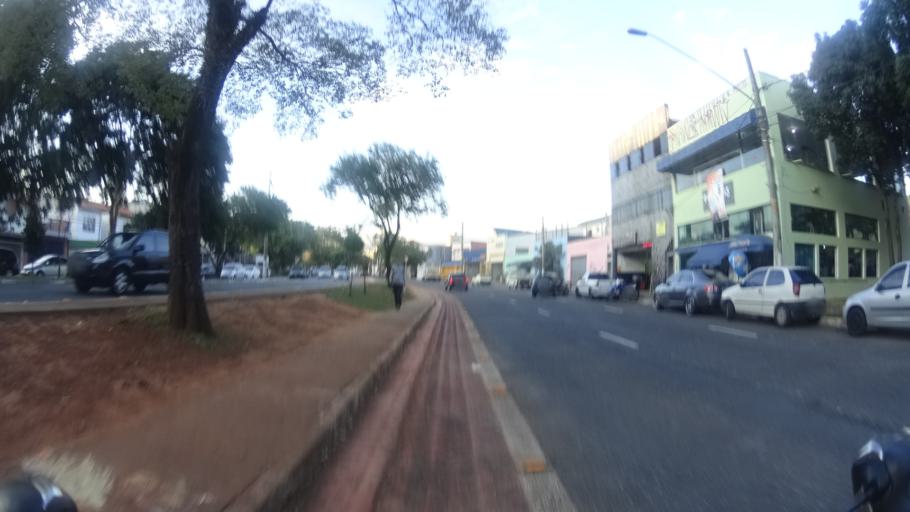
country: BR
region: Sao Paulo
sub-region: Sao Paulo
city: Sao Paulo
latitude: -23.4812
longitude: -46.6291
